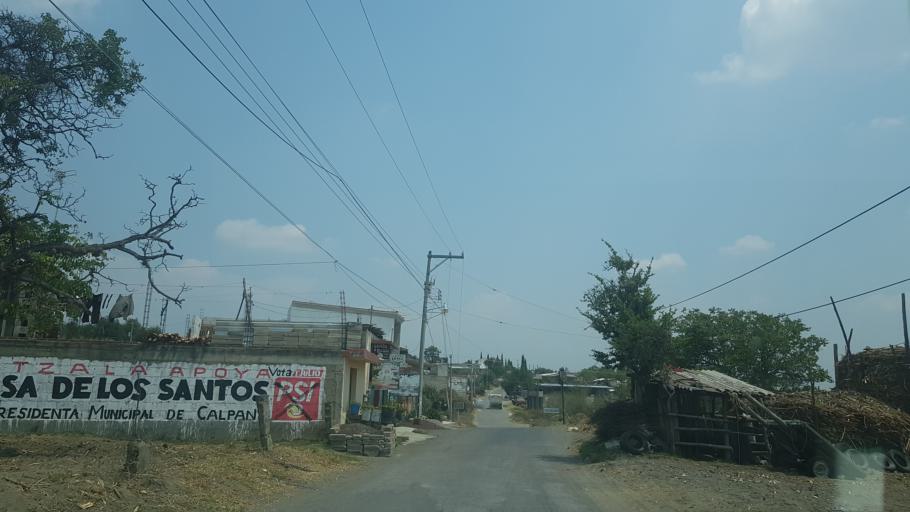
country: MX
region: Puebla
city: San Andres Calpan
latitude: 19.0991
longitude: -98.4761
